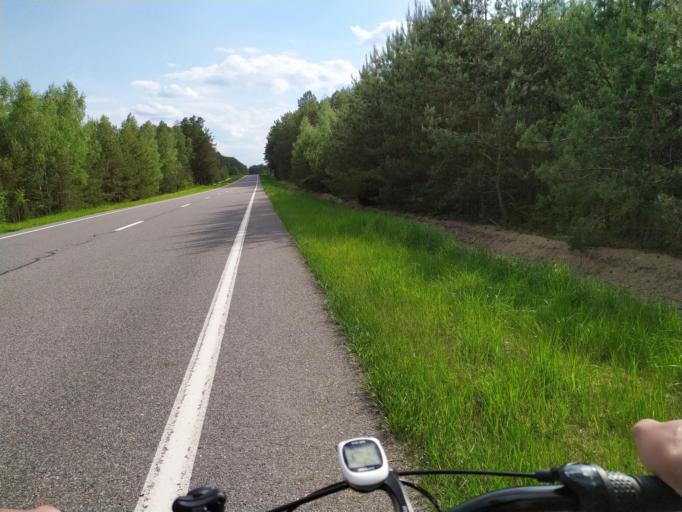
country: BY
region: Brest
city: Zhabinka
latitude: 52.4448
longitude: 24.1349
